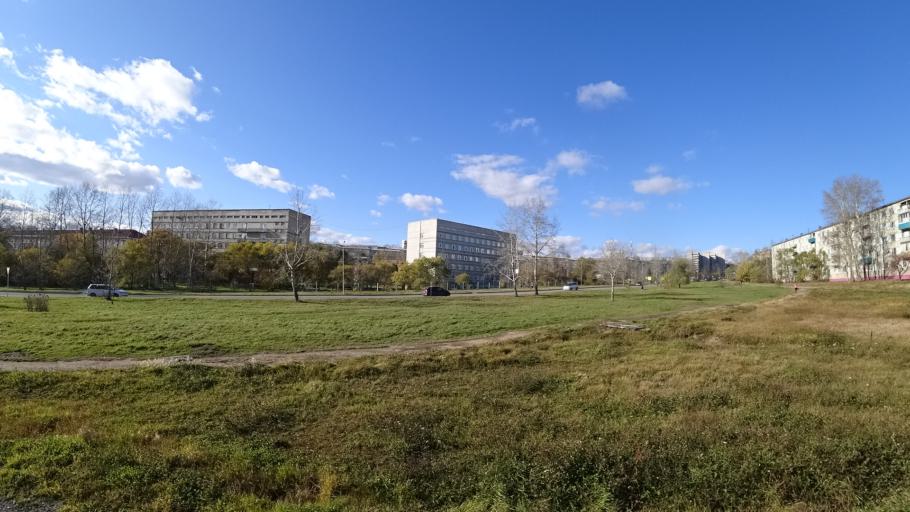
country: RU
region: Khabarovsk Krai
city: Amursk
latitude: 50.2344
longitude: 136.9116
